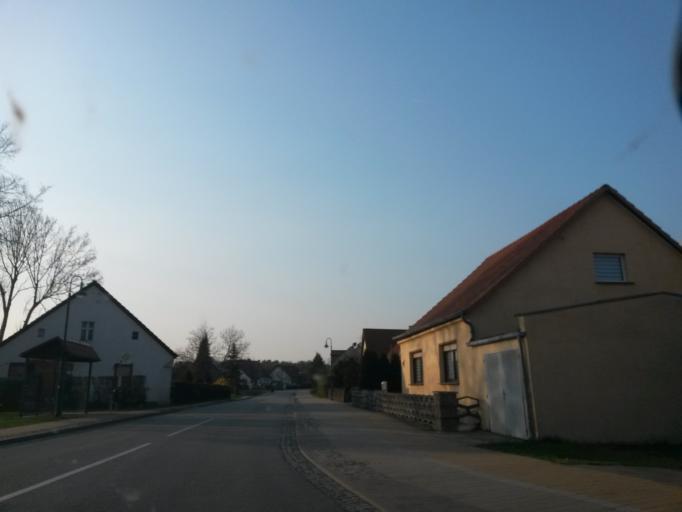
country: DE
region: Brandenburg
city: Rehfelde
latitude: 52.4622
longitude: 13.9091
